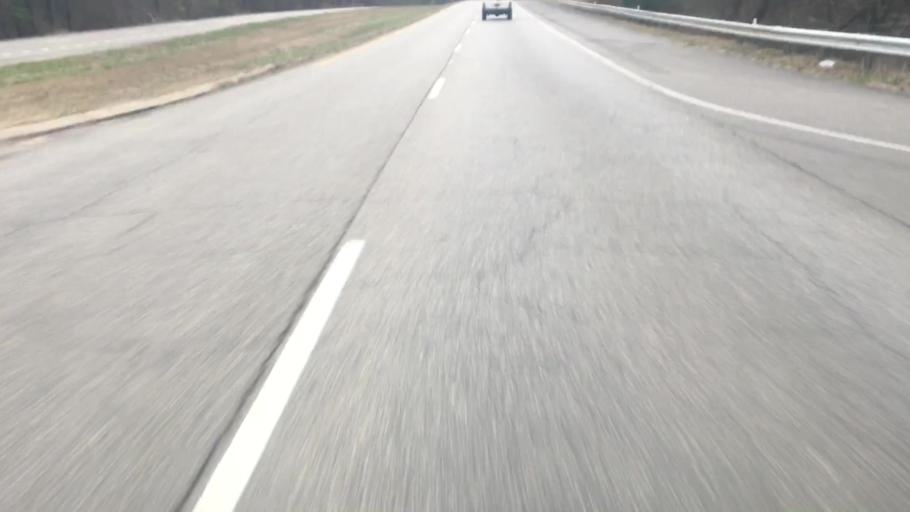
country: US
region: Alabama
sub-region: Walker County
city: Sumiton
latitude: 33.7135
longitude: -86.9954
